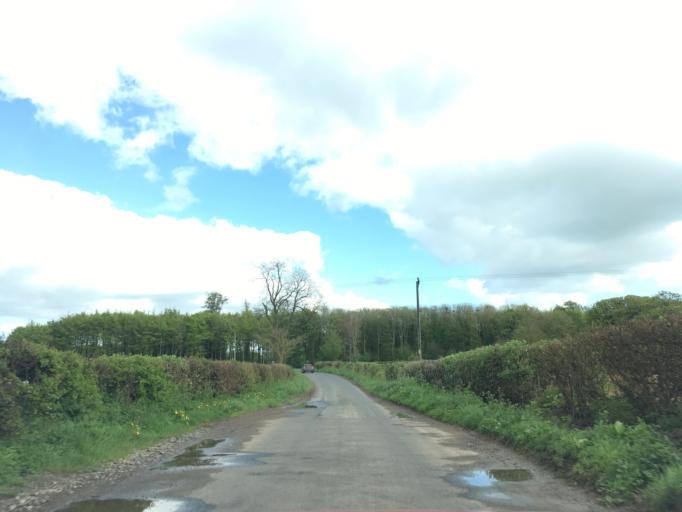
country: GB
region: England
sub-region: Wiltshire
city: Luckington
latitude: 51.5835
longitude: -2.2794
